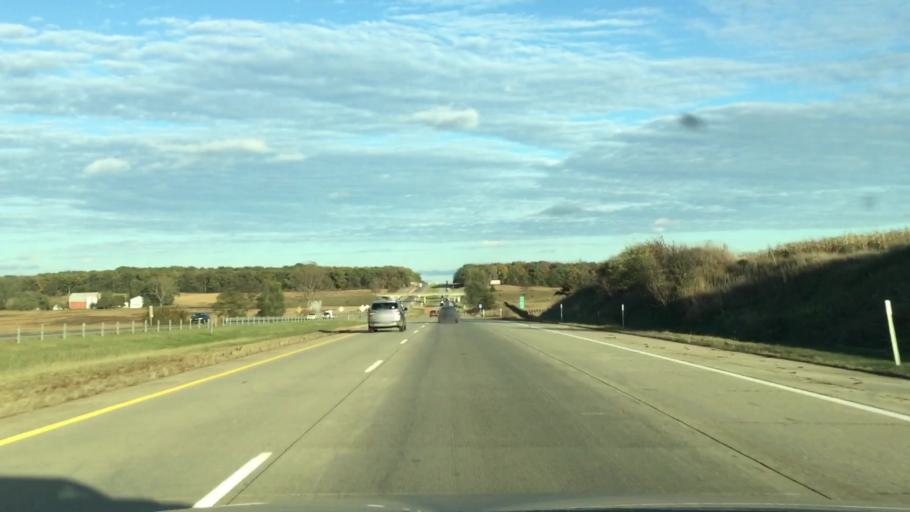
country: US
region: Michigan
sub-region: Calhoun County
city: Marshall
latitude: 42.2830
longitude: -84.8563
